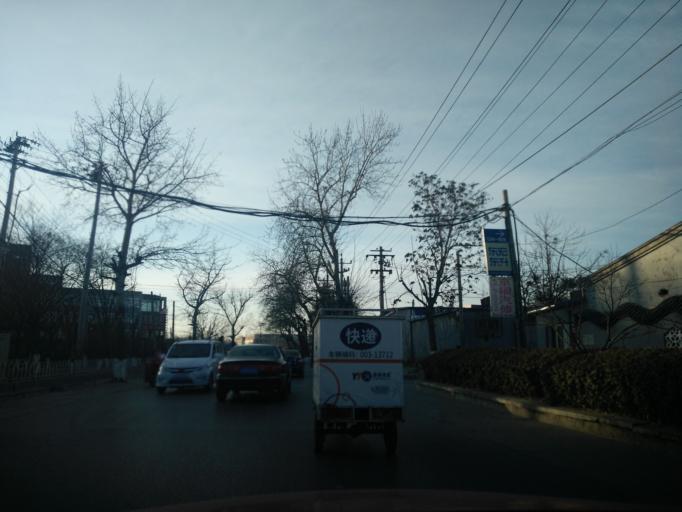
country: CN
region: Beijing
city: Huaxiang
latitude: 39.8202
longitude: 116.3435
